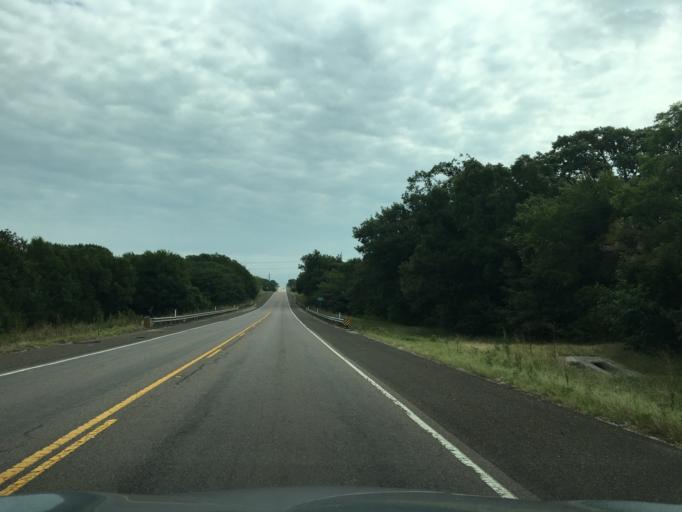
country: US
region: Texas
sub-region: Collin County
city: Anna
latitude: 33.3168
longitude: -96.5057
